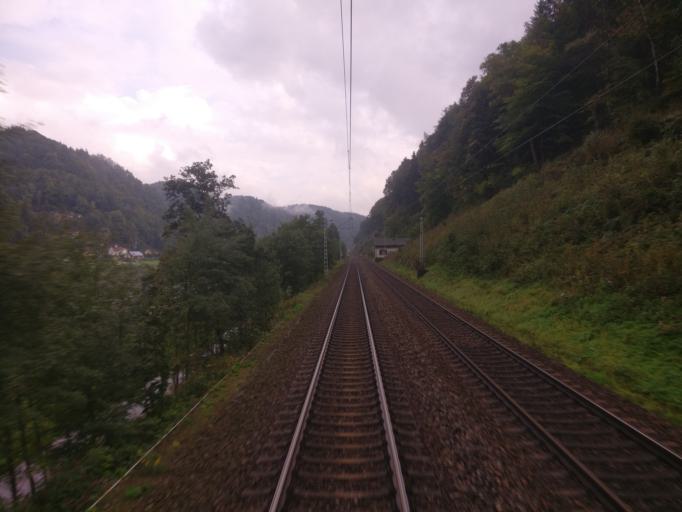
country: DE
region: Saxony
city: Bad Schandau
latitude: 50.8943
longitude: 14.2248
